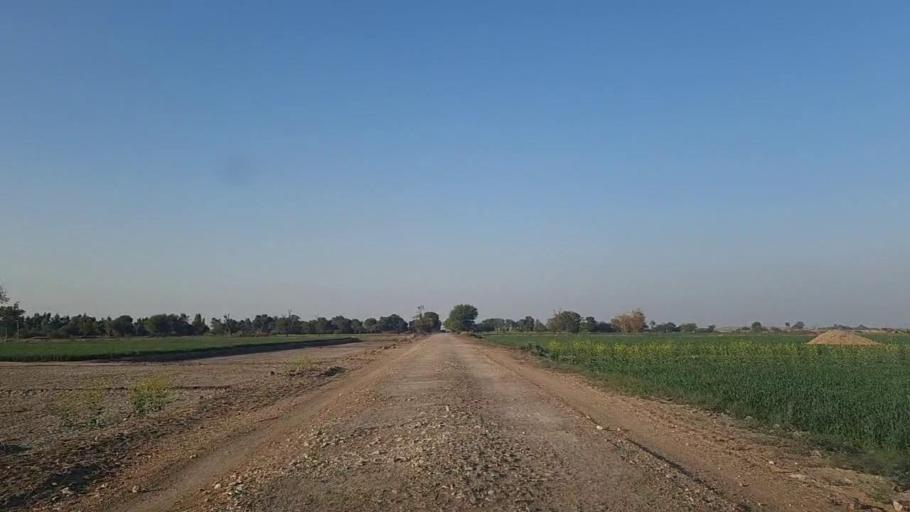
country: PK
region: Sindh
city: Jam Sahib
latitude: 26.3037
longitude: 68.6704
